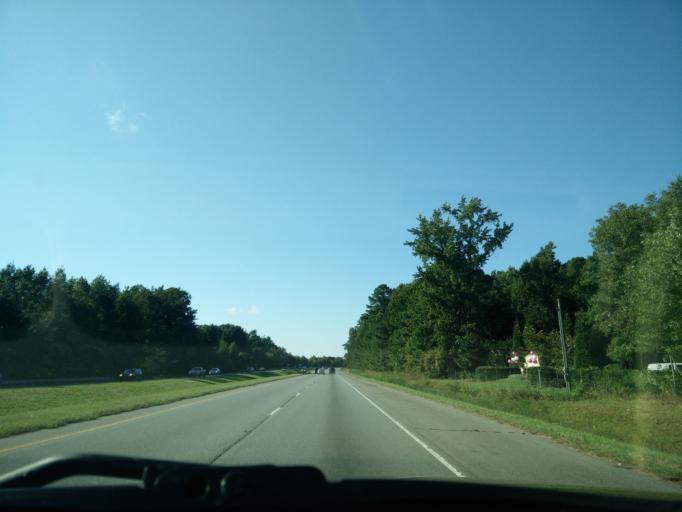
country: US
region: Virginia
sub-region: City of Chesapeake
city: Chesapeake
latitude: 36.7426
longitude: -76.2529
